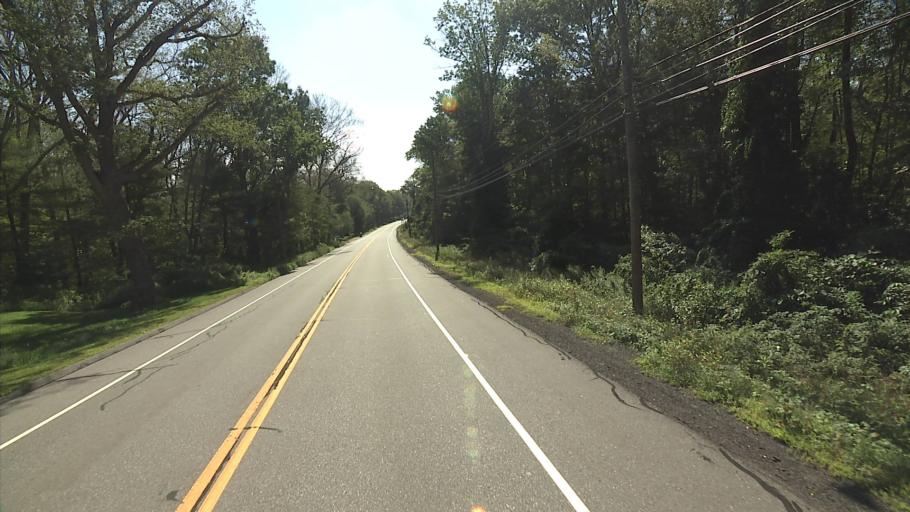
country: US
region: Connecticut
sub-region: Tolland County
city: Crystal Lake
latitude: 41.9756
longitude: -72.3750
